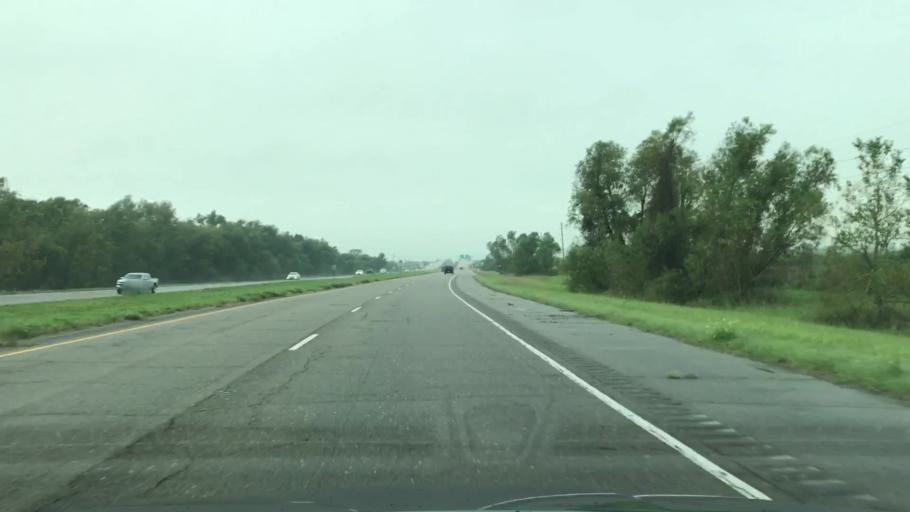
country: US
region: Louisiana
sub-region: Lafourche Parish
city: Mathews
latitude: 29.7184
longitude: -90.5626
